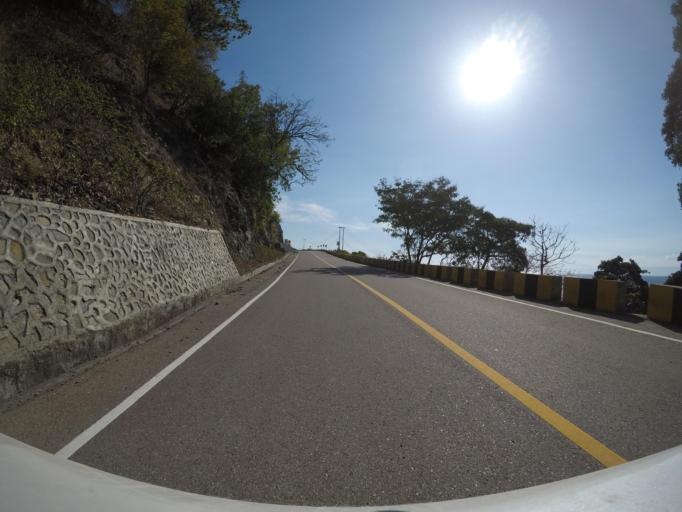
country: TL
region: Liquica
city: Maubara
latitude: -8.6229
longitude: 125.1686
